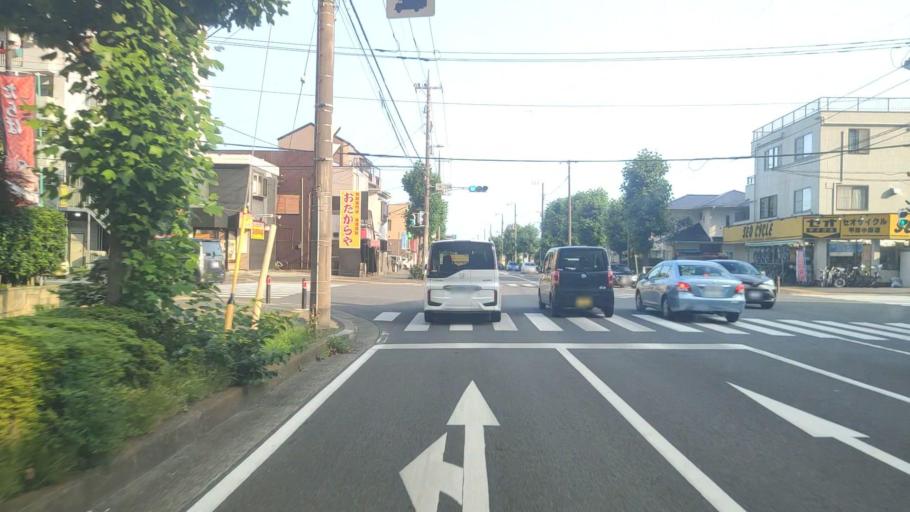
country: JP
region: Kanagawa
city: Hiratsuka
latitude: 35.3445
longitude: 139.3343
